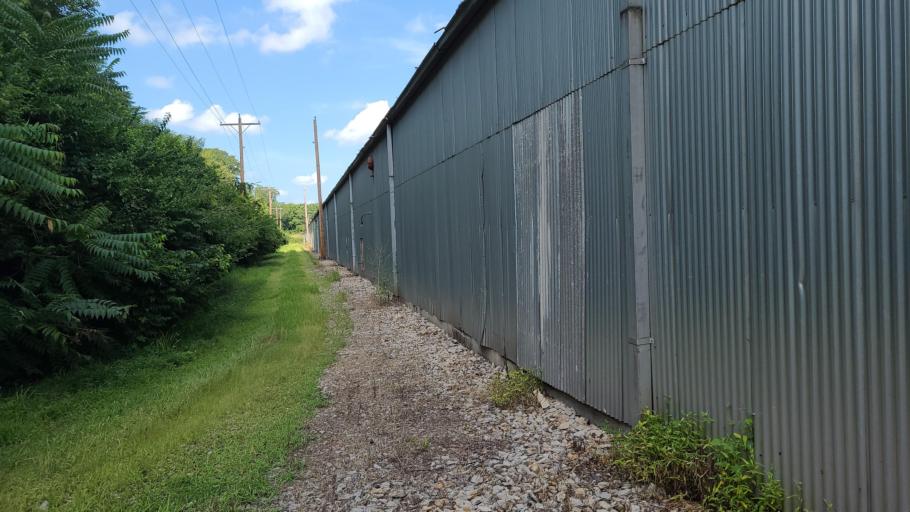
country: US
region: Kansas
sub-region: Douglas County
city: Lawrence
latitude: 38.9554
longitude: -95.2001
